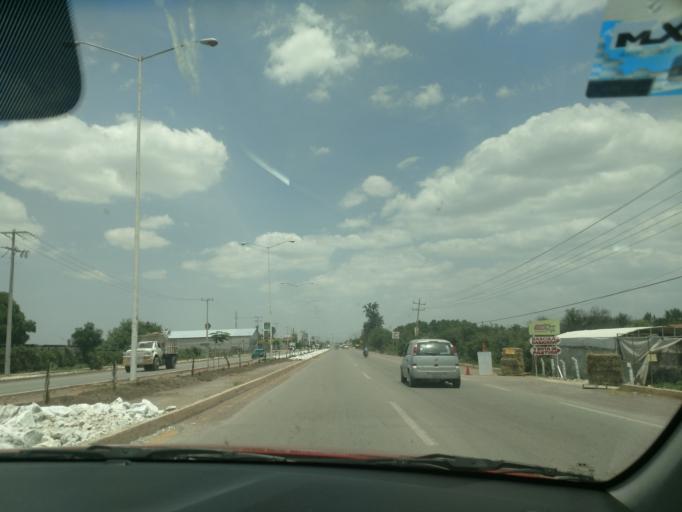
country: MX
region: San Luis Potosi
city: Ciudad Fernandez
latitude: 21.9381
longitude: -100.0329
